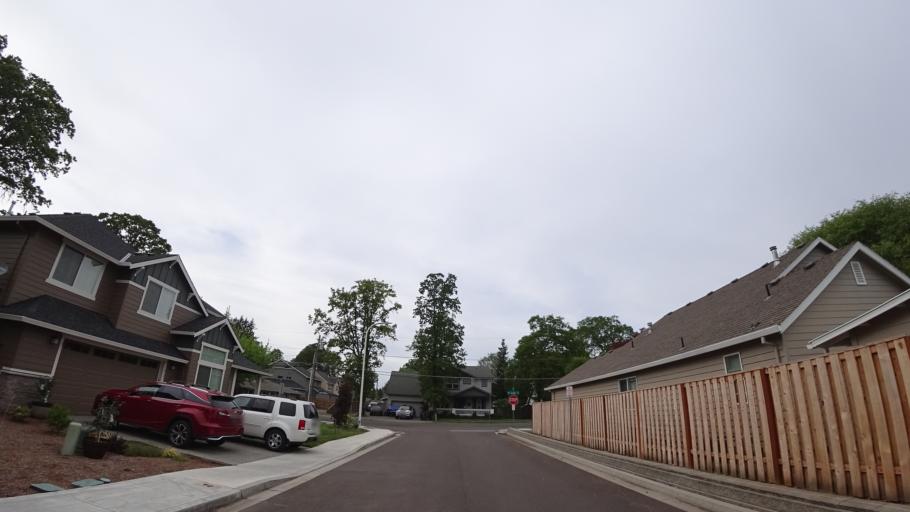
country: US
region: Oregon
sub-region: Washington County
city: Aloha
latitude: 45.5119
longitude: -122.9195
